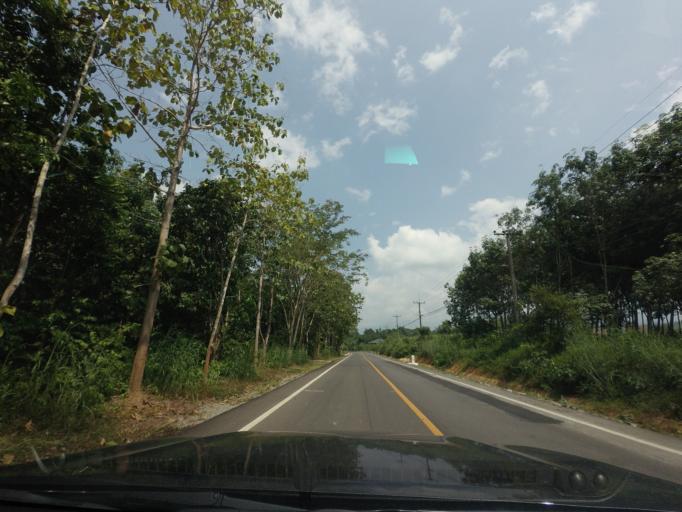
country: TH
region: Nan
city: Santi Suk
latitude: 18.9791
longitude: 100.9307
